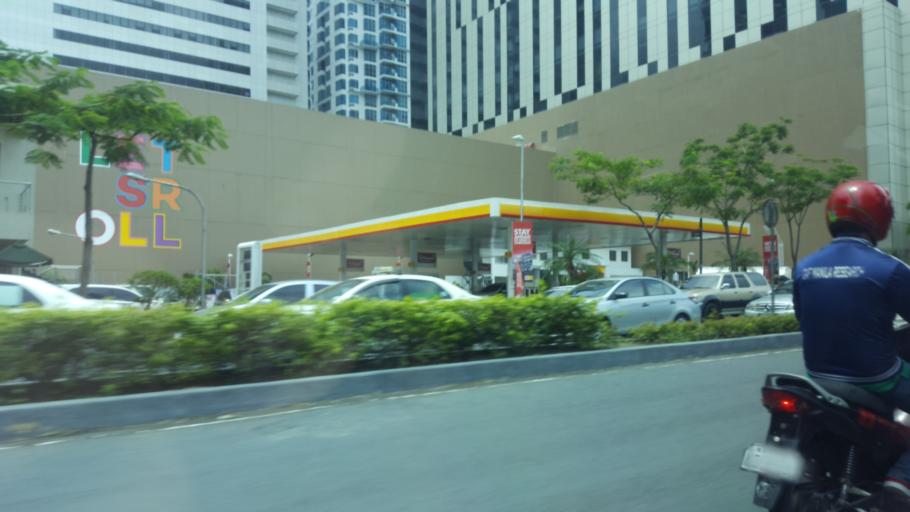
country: PH
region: Metro Manila
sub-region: Makati City
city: Makati City
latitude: 14.5550
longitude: 121.0462
